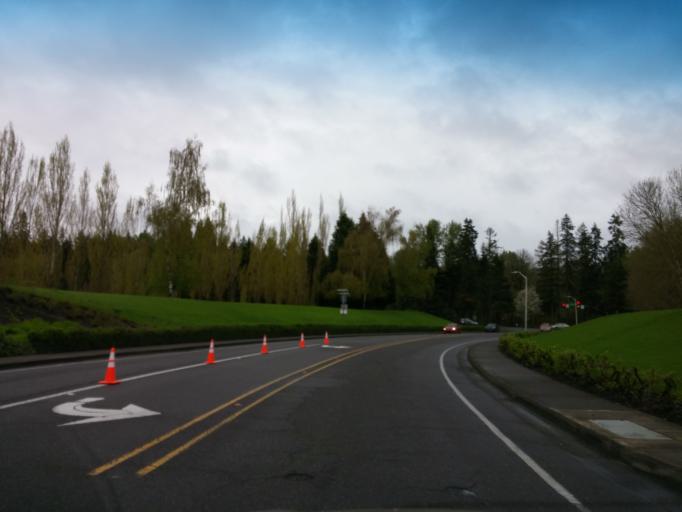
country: US
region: Oregon
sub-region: Washington County
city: Cedar Mill
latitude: 45.5072
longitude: -122.8332
